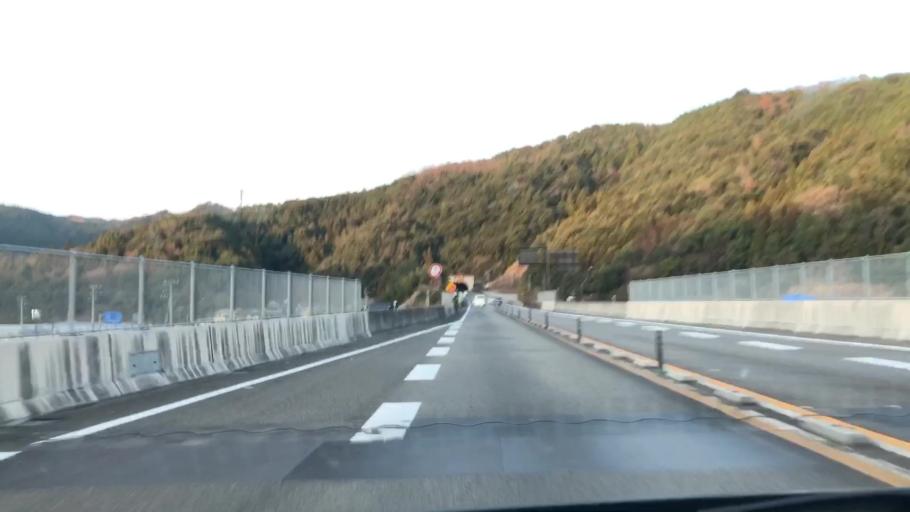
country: JP
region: Kumamoto
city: Minamata
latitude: 32.2999
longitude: 130.5098
